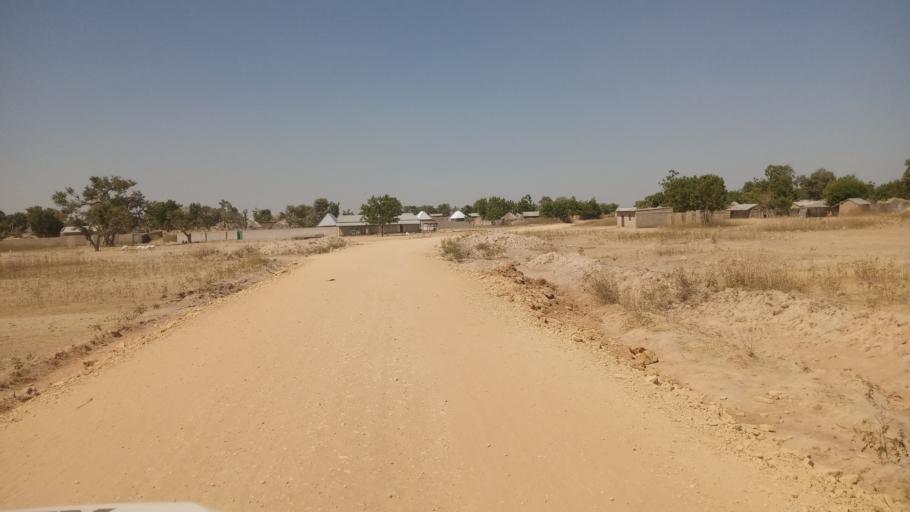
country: NG
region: Adamawa
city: Ngurore
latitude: 9.2978
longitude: 12.1381
